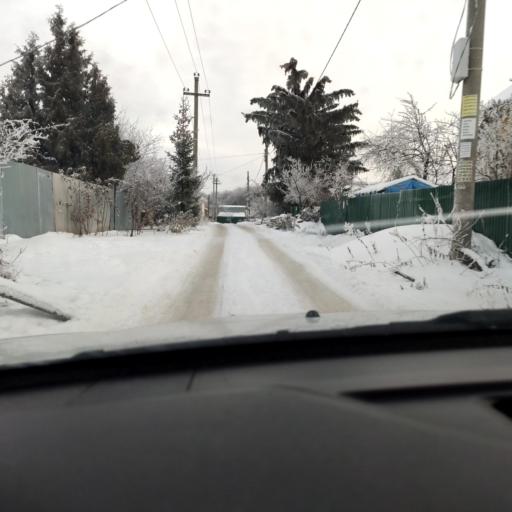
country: RU
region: Samara
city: Petra-Dubrava
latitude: 53.3012
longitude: 50.2504
